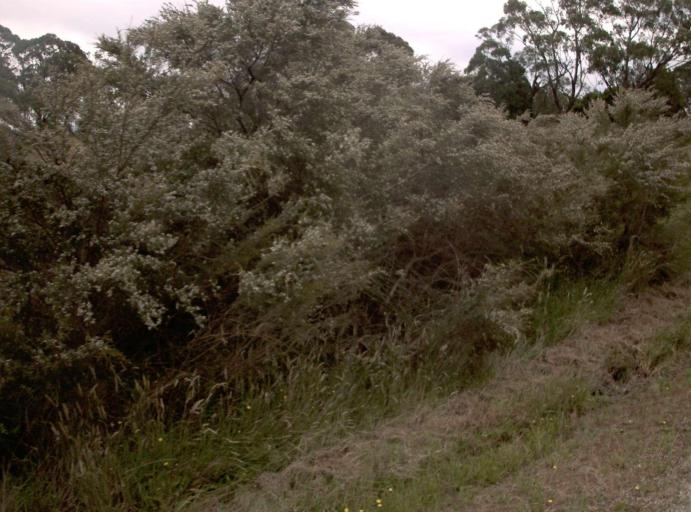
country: AU
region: Victoria
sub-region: East Gippsland
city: Bairnsdale
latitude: -37.8813
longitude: 147.5588
